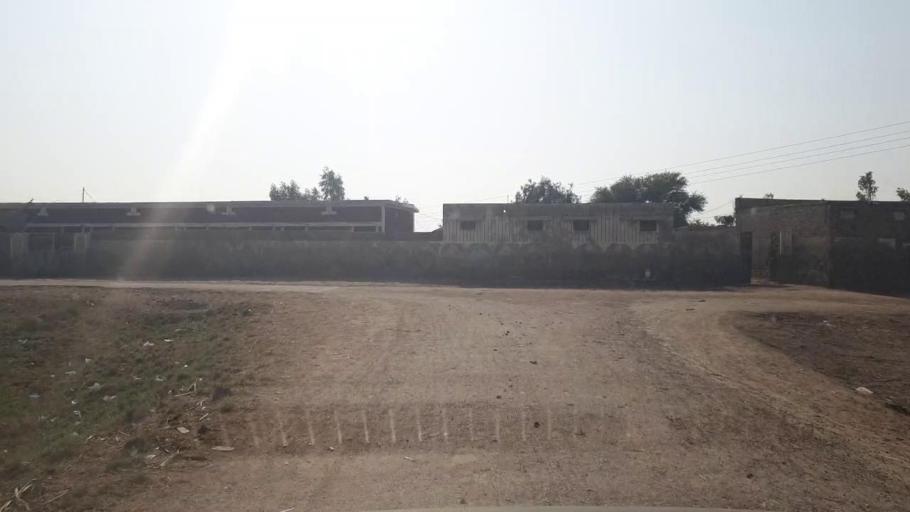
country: PK
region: Sindh
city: Bhit Shah
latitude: 25.8101
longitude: 68.5787
